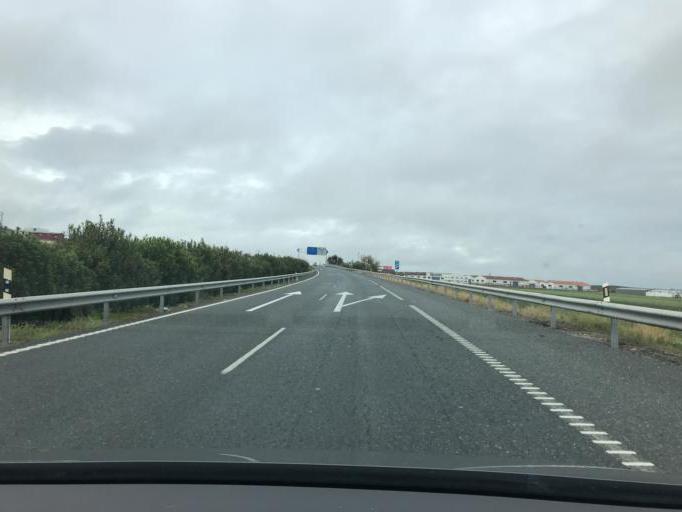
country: ES
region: Andalusia
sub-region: Provincia de Sevilla
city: El Arahal
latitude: 37.2540
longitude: -5.5413
